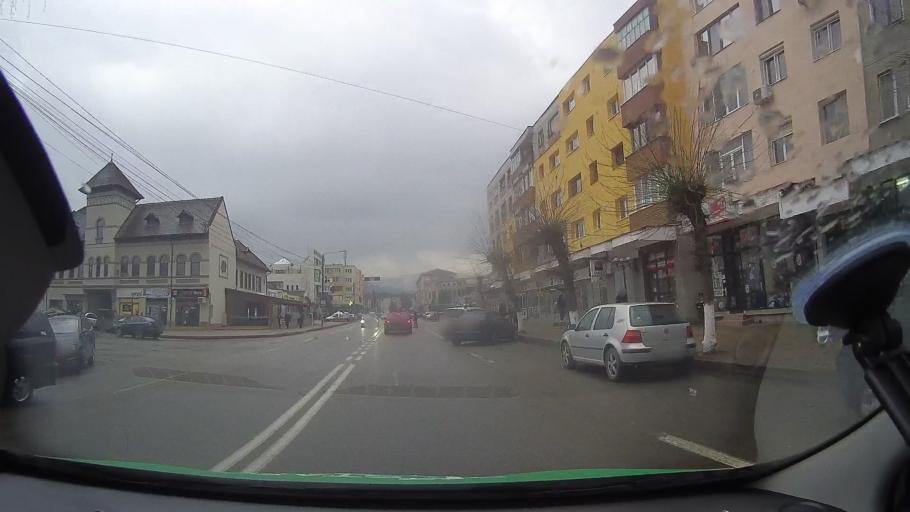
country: RO
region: Hunedoara
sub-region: Municipiul Brad
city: Brad
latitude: 46.1303
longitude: 22.7912
